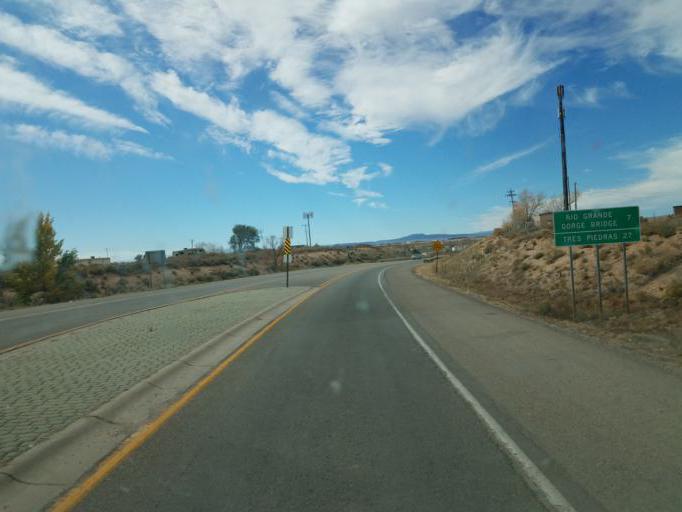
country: US
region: New Mexico
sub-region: Taos County
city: Taos
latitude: 36.4574
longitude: -105.5974
